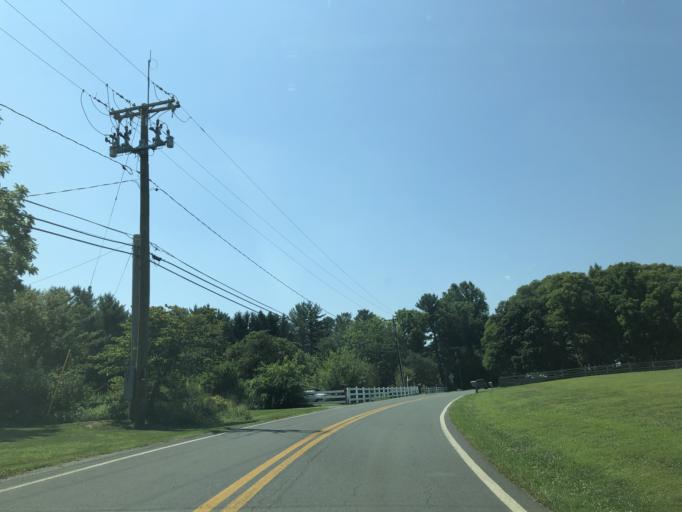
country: US
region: Maryland
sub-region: Carroll County
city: Eldersburg
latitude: 39.4464
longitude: -76.9590
